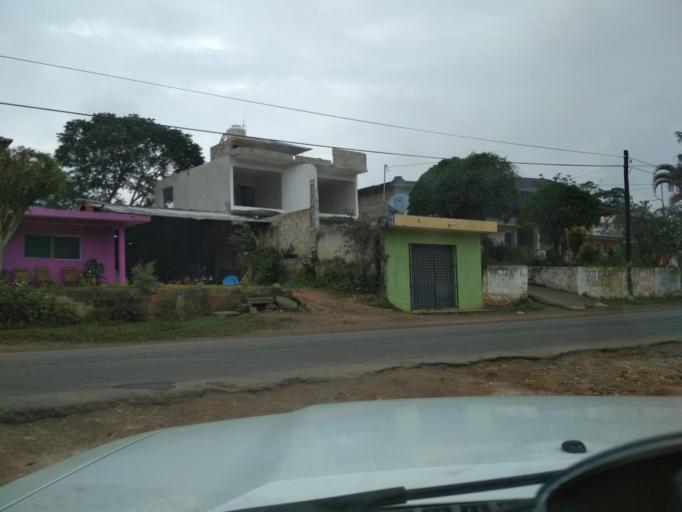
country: MX
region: Veracruz
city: El Castillo
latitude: 19.5630
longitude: -96.8595
